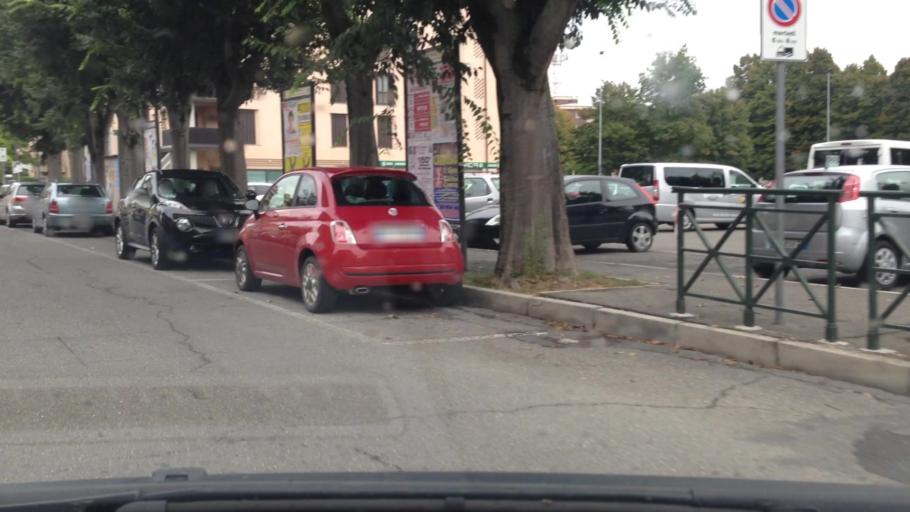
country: IT
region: Piedmont
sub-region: Provincia di Alessandria
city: Tortona
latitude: 44.8964
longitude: 8.8601
